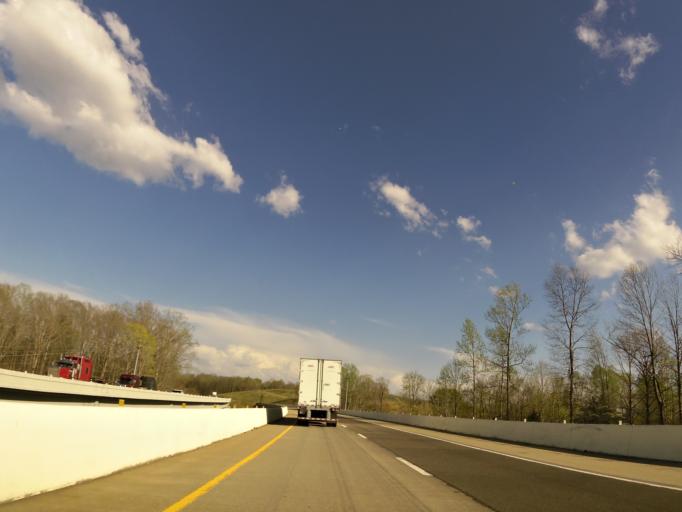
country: US
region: Tennessee
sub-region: Williamson County
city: Thompson's Station
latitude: 35.8270
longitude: -87.0561
